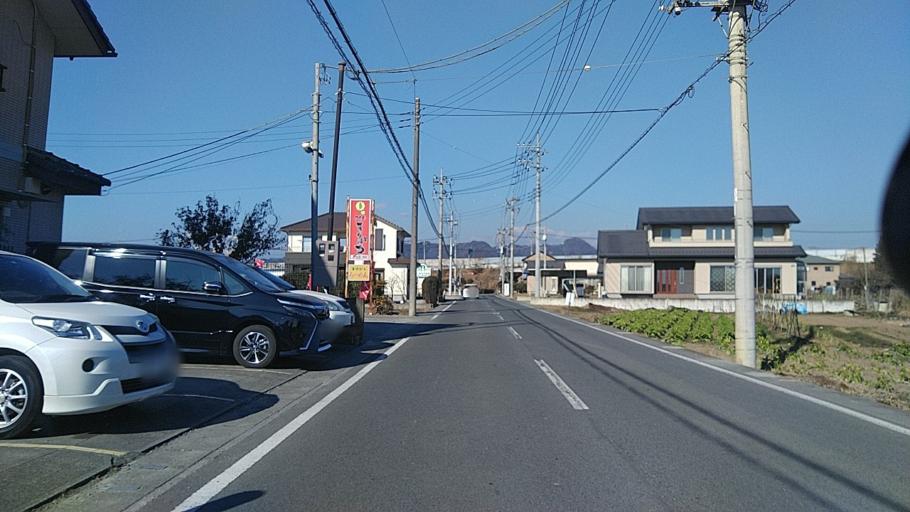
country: JP
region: Tochigi
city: Tanuma
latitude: 36.3628
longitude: 139.5596
